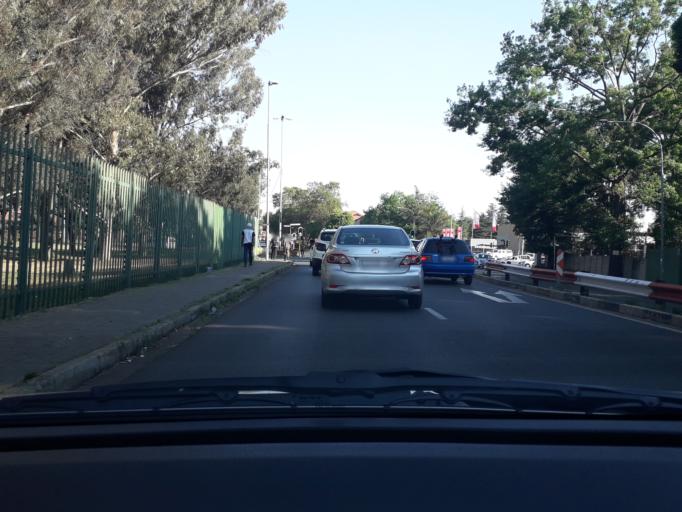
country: ZA
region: Gauteng
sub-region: City of Johannesburg Metropolitan Municipality
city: Johannesburg
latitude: -26.1833
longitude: 28.1048
